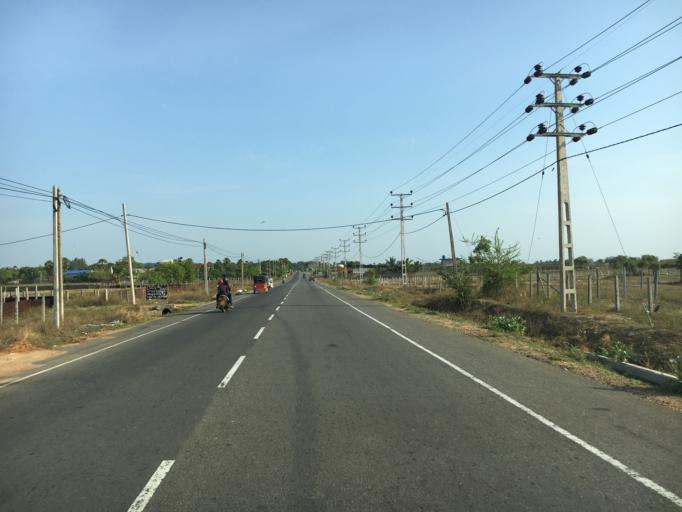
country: LK
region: Eastern Province
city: Eravur Town
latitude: 7.9352
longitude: 81.5102
